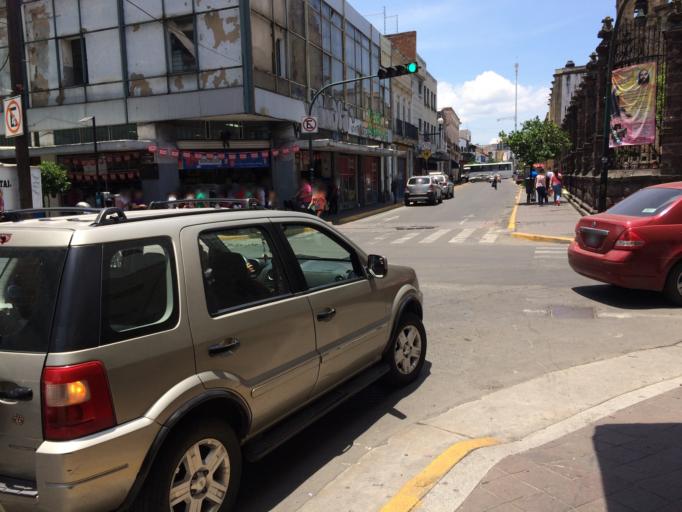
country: MX
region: Jalisco
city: Guadalajara
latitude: 20.6764
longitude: -103.3513
